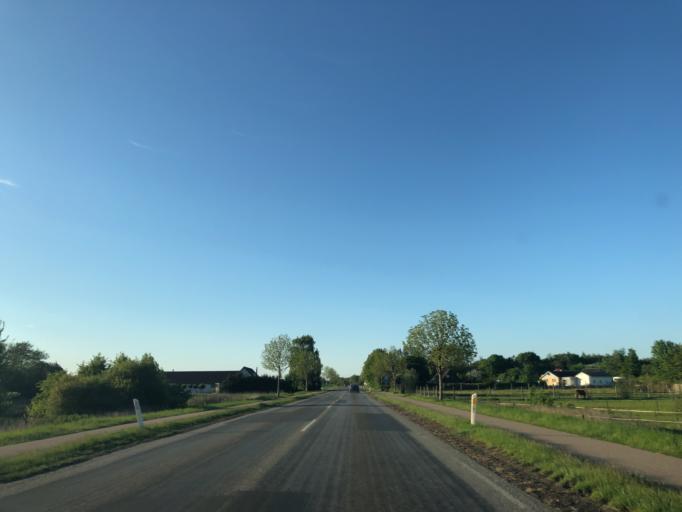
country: DK
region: Zealand
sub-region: Stevns Kommune
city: Harlev
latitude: 55.3701
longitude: 12.2566
